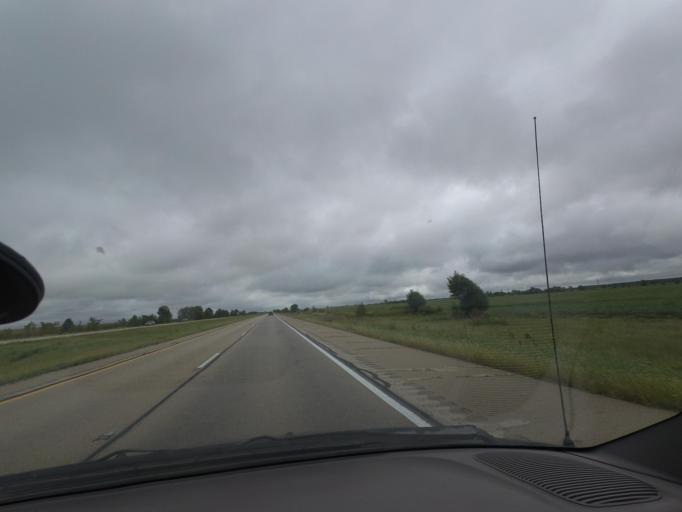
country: US
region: Illinois
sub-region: Piatt County
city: Monticello
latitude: 40.0253
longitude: -88.6766
